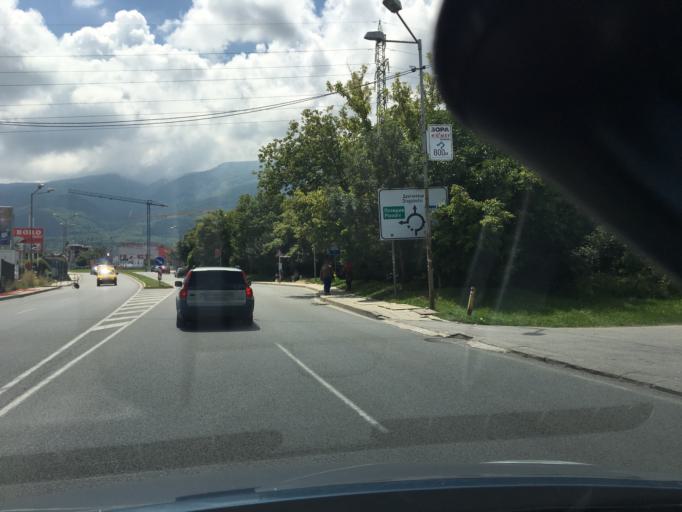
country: BG
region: Sofia-Capital
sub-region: Stolichna Obshtina
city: Sofia
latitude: 42.6434
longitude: 23.3132
